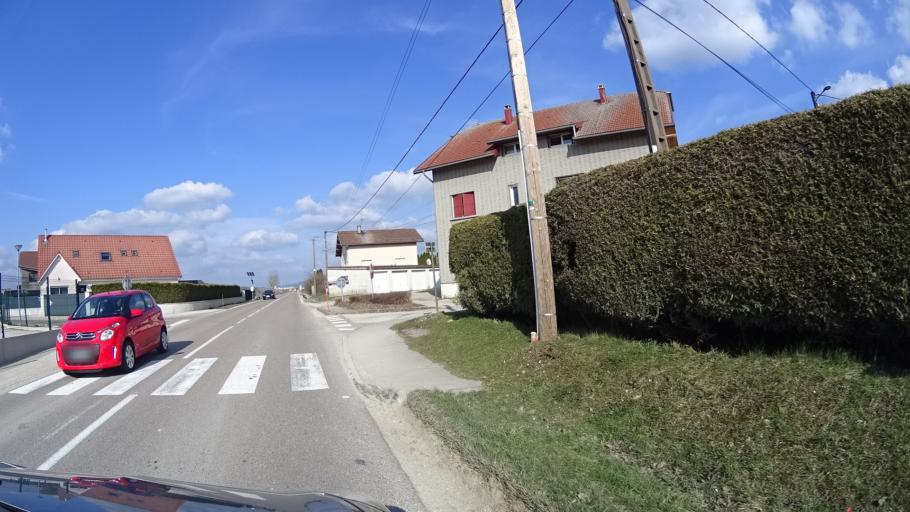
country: FR
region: Franche-Comte
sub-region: Departement du Doubs
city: Doubs
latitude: 46.9156
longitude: 6.3163
